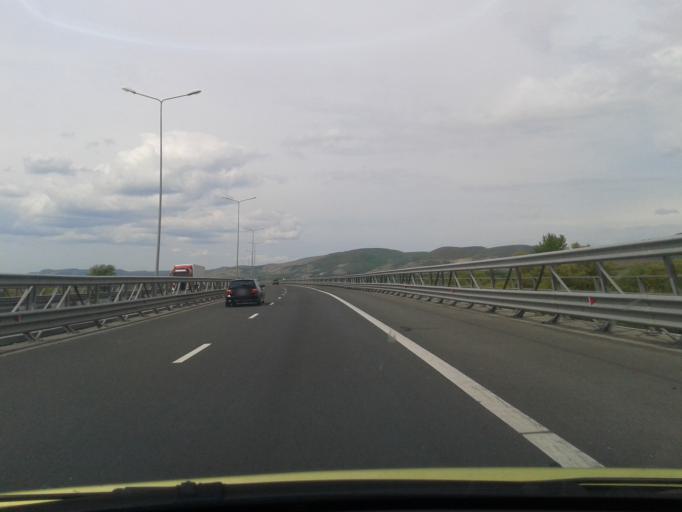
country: RO
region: Hunedoara
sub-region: Oras Simeria
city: Simeria
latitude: 45.8647
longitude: 23.0250
